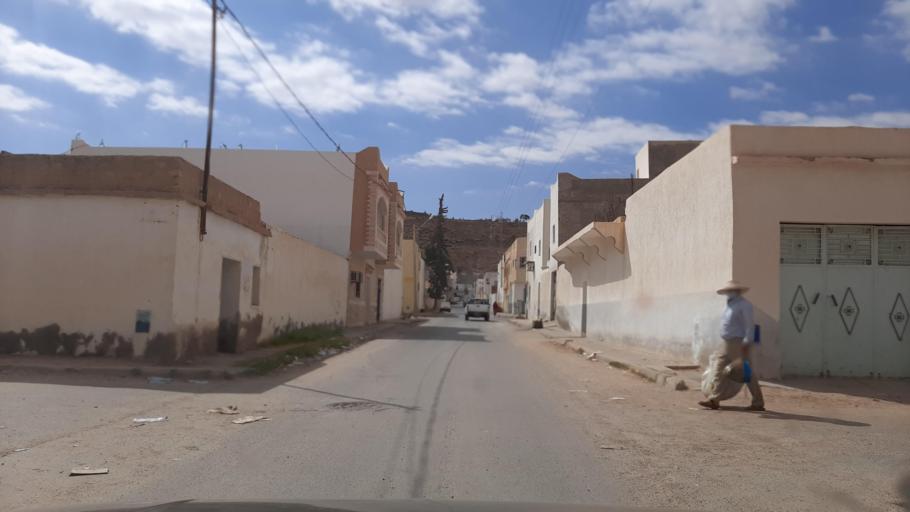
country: TN
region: Tataouine
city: Tataouine
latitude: 32.9278
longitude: 10.4564
